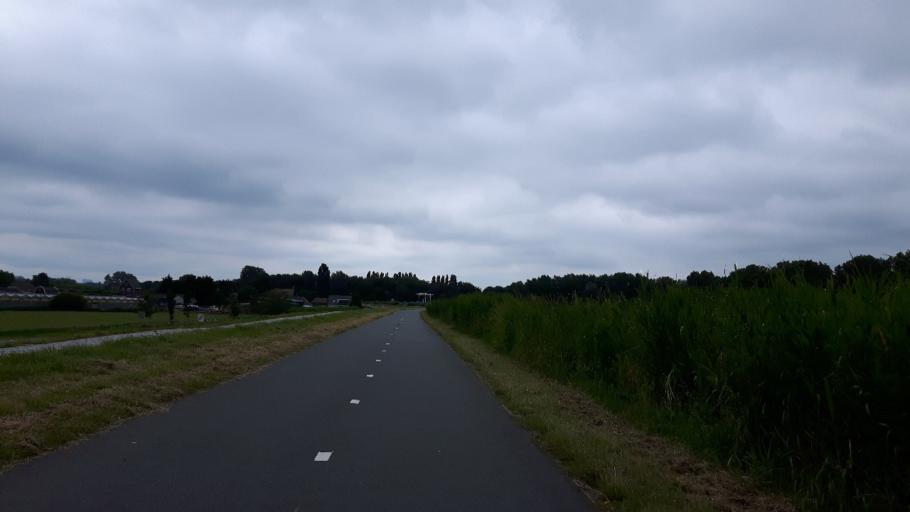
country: NL
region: South Holland
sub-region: Gemeente Lansingerland
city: Bleiswijk
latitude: 51.9934
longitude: 4.5513
